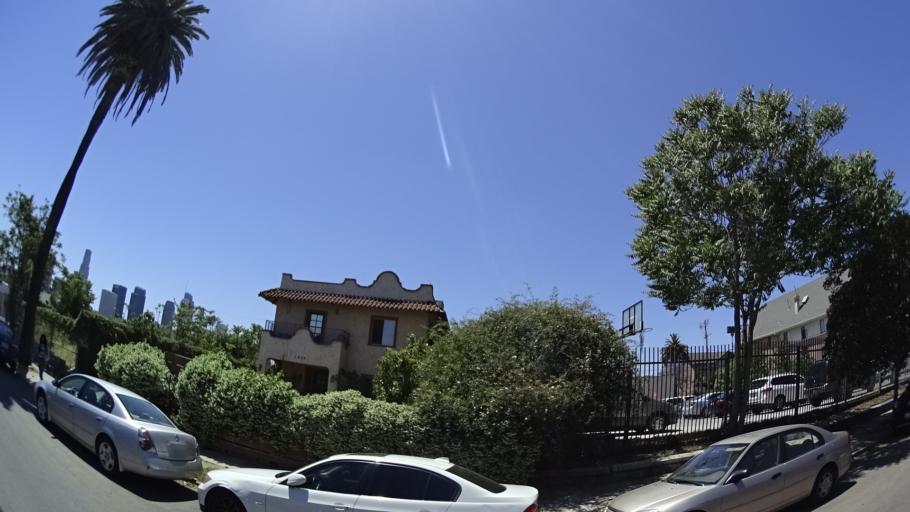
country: US
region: California
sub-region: Los Angeles County
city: Echo Park
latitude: 34.0650
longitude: -118.2638
